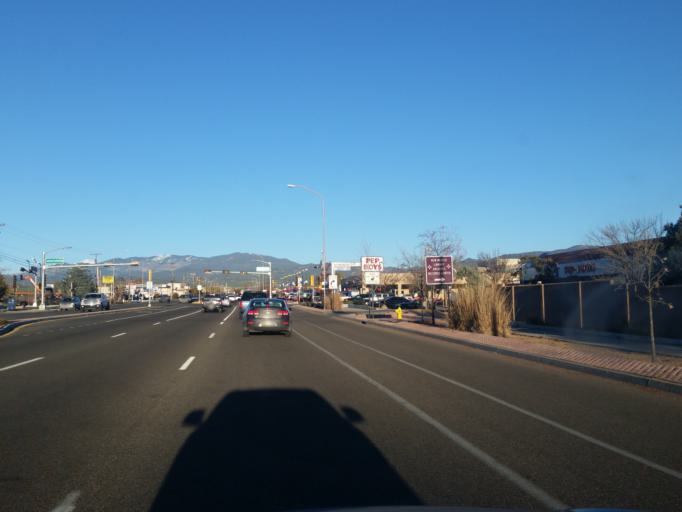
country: US
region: New Mexico
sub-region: Santa Fe County
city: Agua Fria
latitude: 35.6574
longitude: -105.9873
